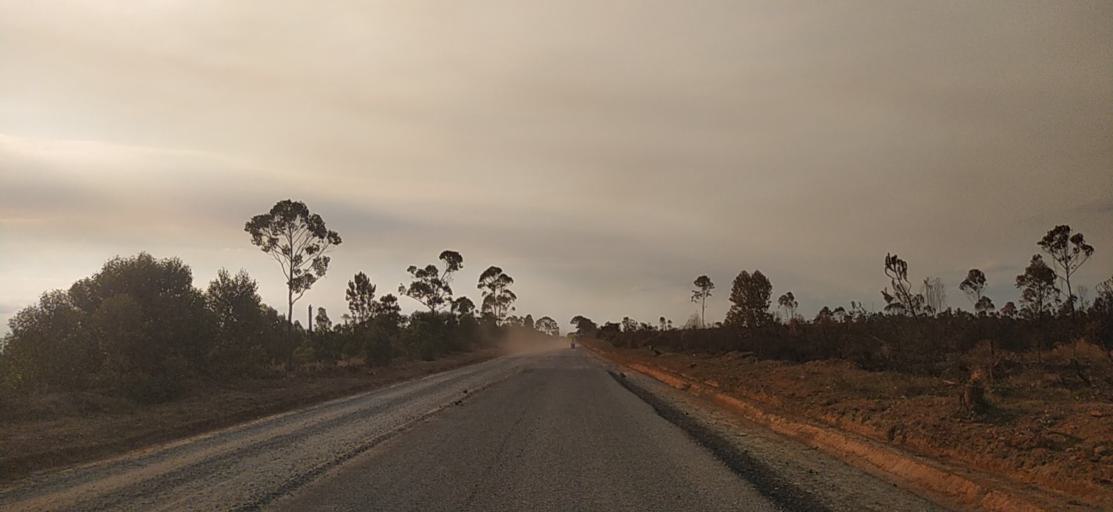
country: MG
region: Alaotra Mangoro
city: Moramanga
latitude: -18.5731
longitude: 48.2677
